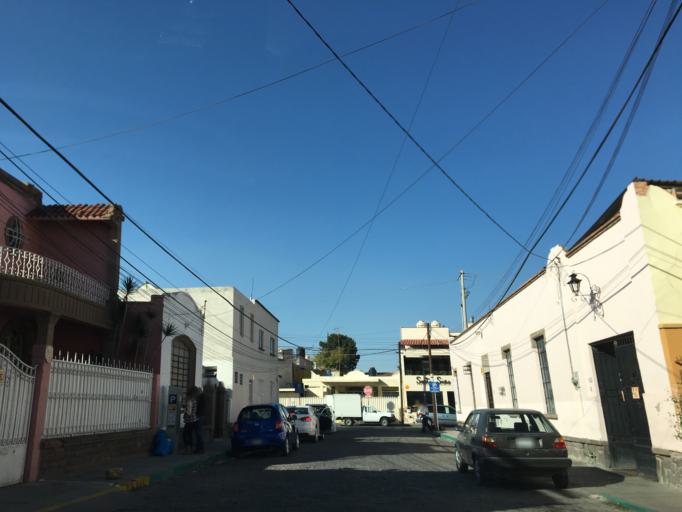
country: MX
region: San Luis Potosi
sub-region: San Luis Potosi
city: San Luis Potosi
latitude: 22.1505
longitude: -100.9940
